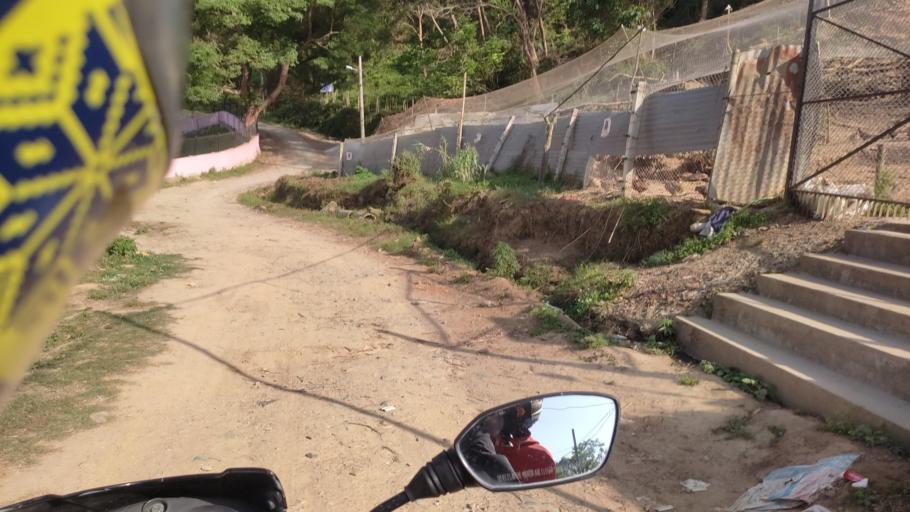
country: NP
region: Central Region
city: Kirtipur
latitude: 27.6564
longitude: 85.2665
